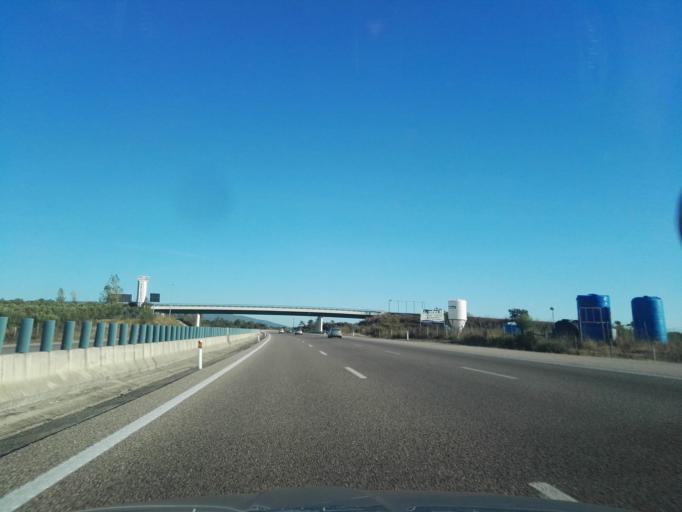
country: PT
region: Santarem
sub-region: Alcanena
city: Alcanena
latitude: 39.4196
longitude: -8.6321
